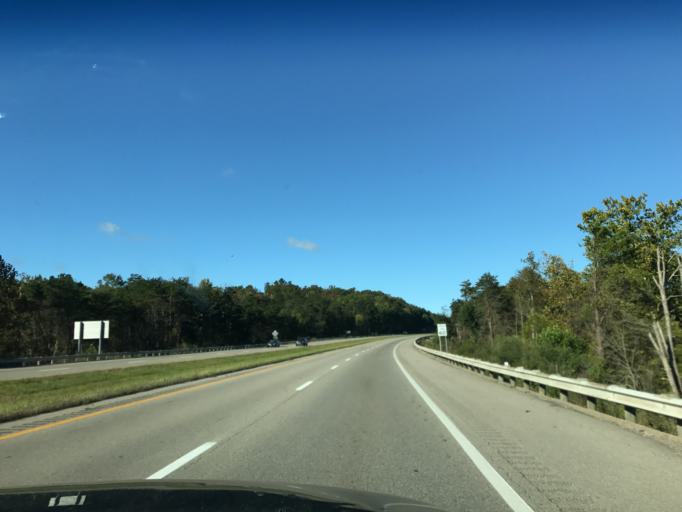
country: US
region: West Virginia
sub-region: Wood County
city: Washington
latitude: 39.2373
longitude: -81.7458
